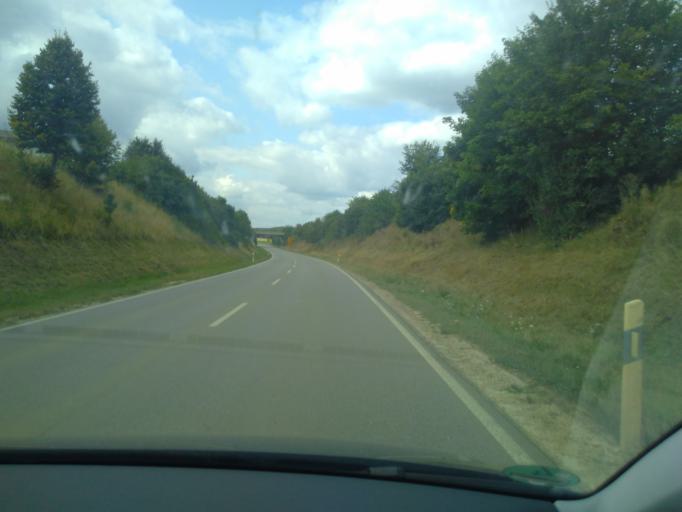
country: DE
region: Baden-Wuerttemberg
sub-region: Tuebingen Region
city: Merklingen
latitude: 48.5157
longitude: 9.7511
